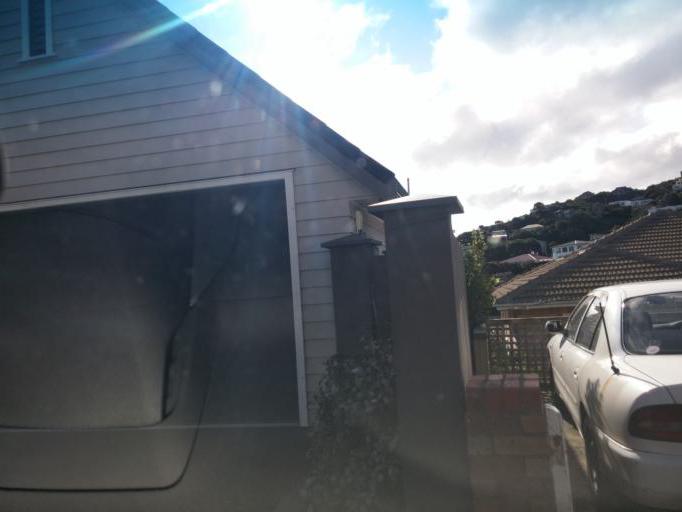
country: NZ
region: Wellington
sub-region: Wellington City
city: Wellington
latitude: -41.3254
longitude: 174.8249
